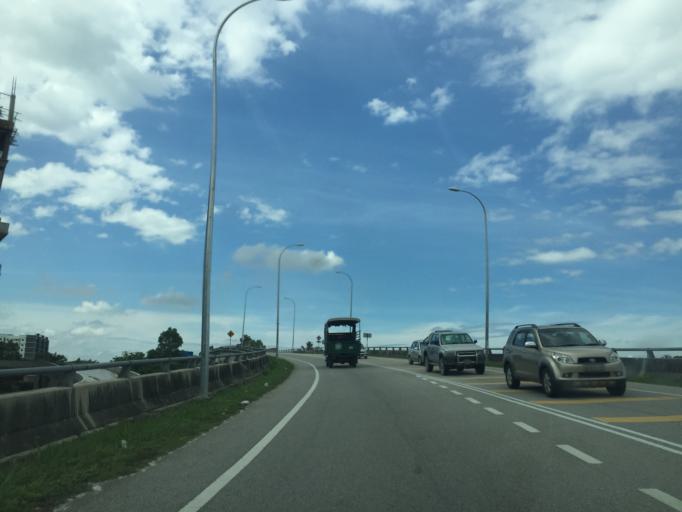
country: MY
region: Perak
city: Kampar
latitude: 4.3280
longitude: 101.1325
